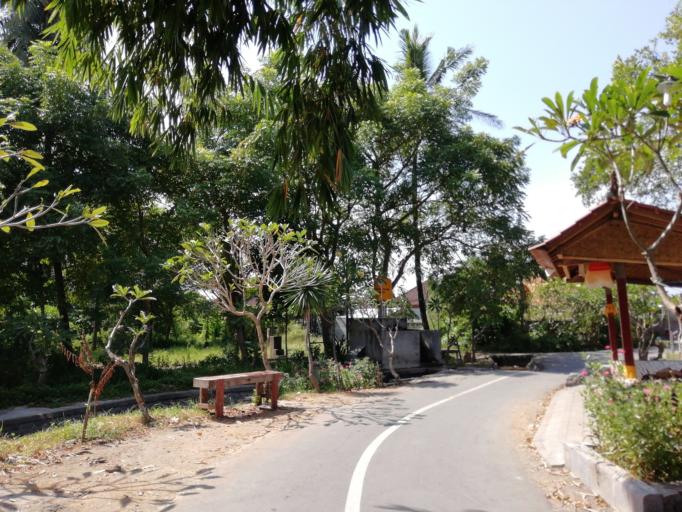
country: ID
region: Bali
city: Banjar Pasekan
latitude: -8.6095
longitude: 115.2860
